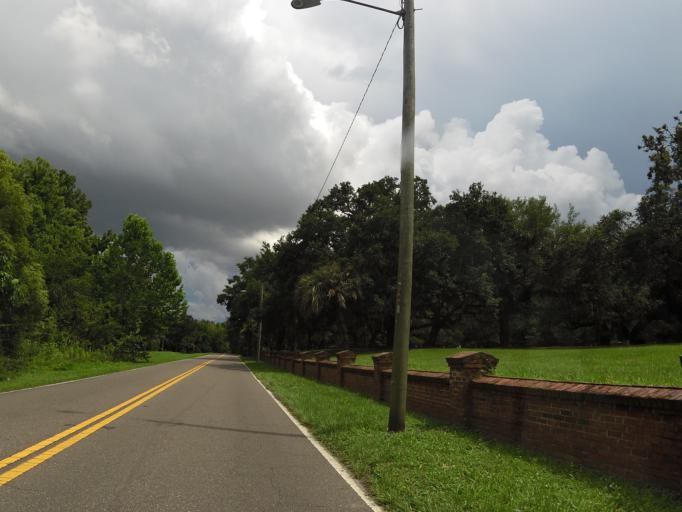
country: US
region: Florida
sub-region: Duval County
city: Jacksonville
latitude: 30.3695
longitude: -81.6419
